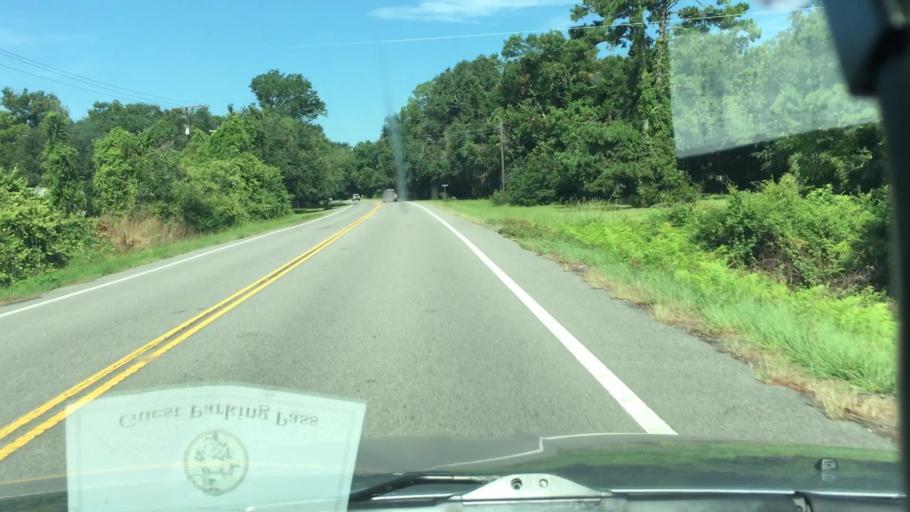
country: US
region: South Carolina
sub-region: Beaufort County
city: Beaufort
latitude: 32.4148
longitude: -80.4836
